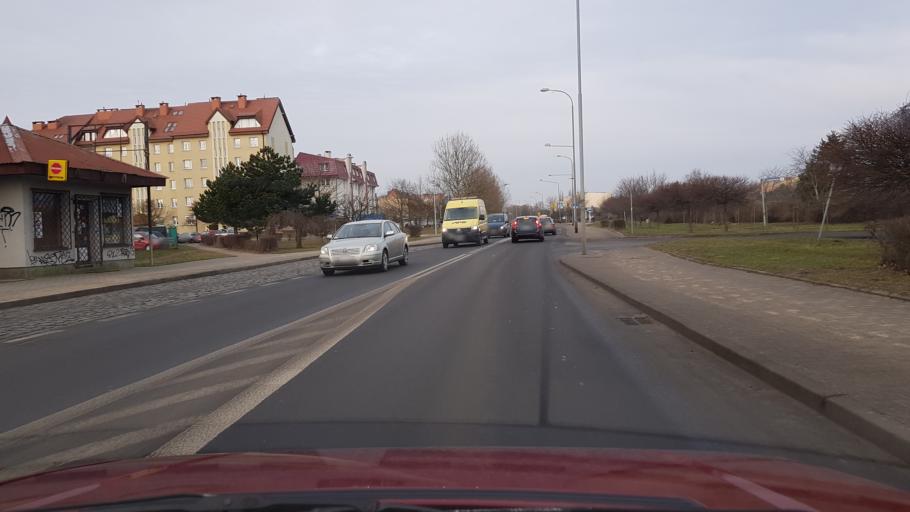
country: PL
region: West Pomeranian Voivodeship
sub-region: Powiat policki
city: Police
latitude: 53.5430
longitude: 14.5657
